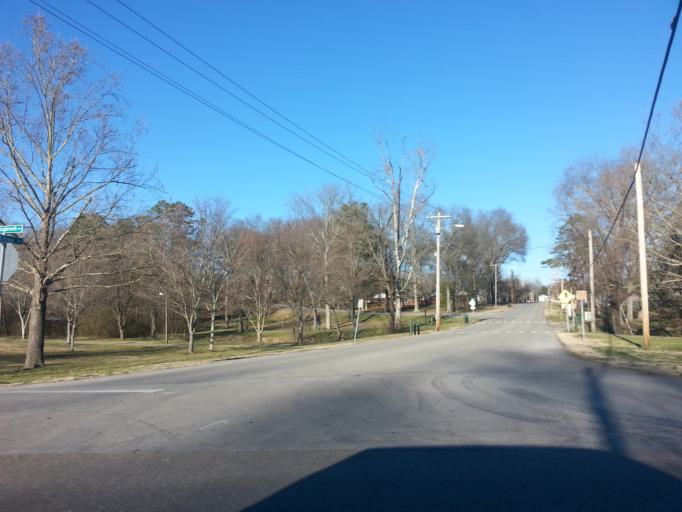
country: US
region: Tennessee
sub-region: Blount County
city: Alcoa
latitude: 35.7984
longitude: -83.9813
